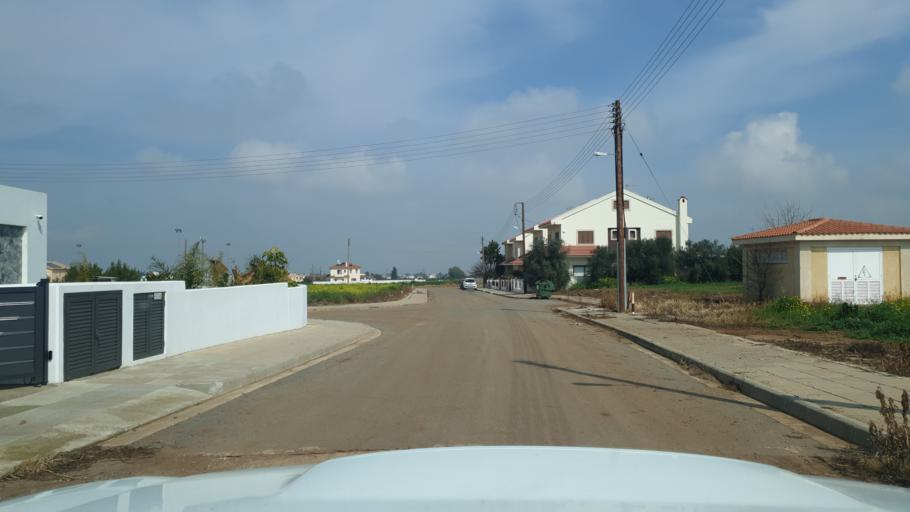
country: CY
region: Lefkosia
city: Kato Deftera
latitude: 35.0808
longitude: 33.2889
